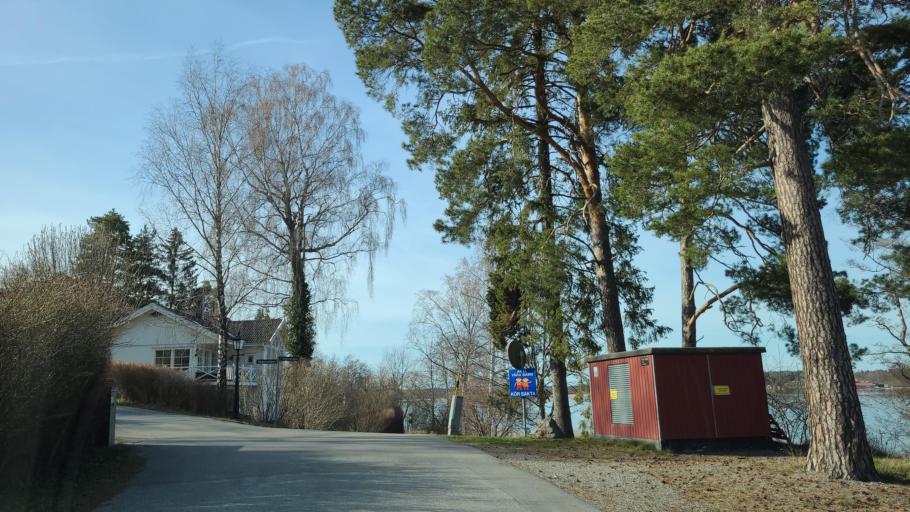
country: SE
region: Stockholm
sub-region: Ekero Kommun
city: Ekeroe
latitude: 59.2893
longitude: 17.7638
